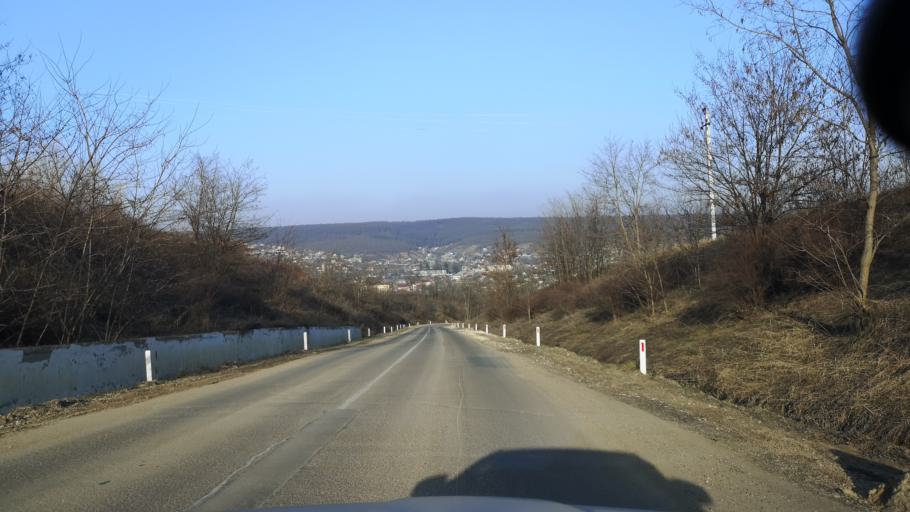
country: MD
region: Stinga Nistrului
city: Bucovat
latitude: 47.1069
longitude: 28.4985
